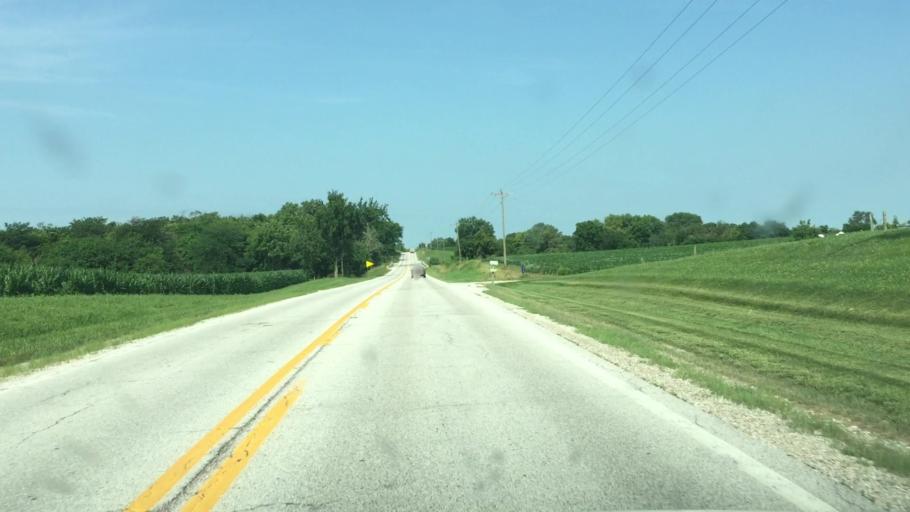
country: US
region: Illinois
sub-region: Hancock County
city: Nauvoo
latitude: 40.5515
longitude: -91.3120
